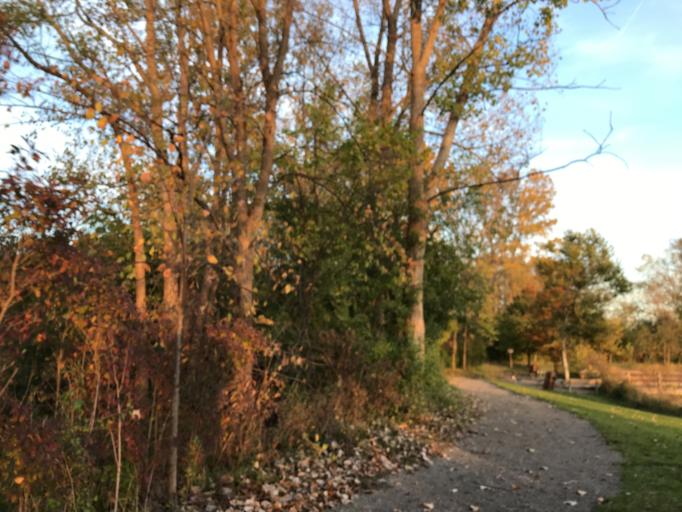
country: US
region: Michigan
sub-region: Oakland County
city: Farmington
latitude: 42.4418
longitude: -83.4002
